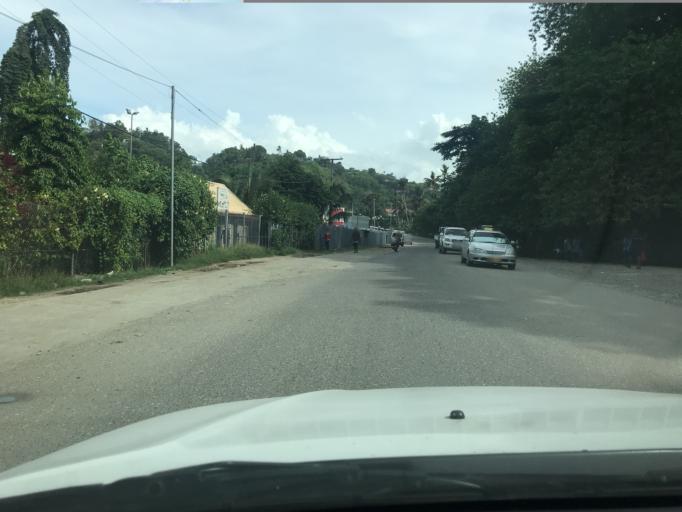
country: SB
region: Guadalcanal
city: Honiara
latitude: -9.4367
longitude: 159.9641
